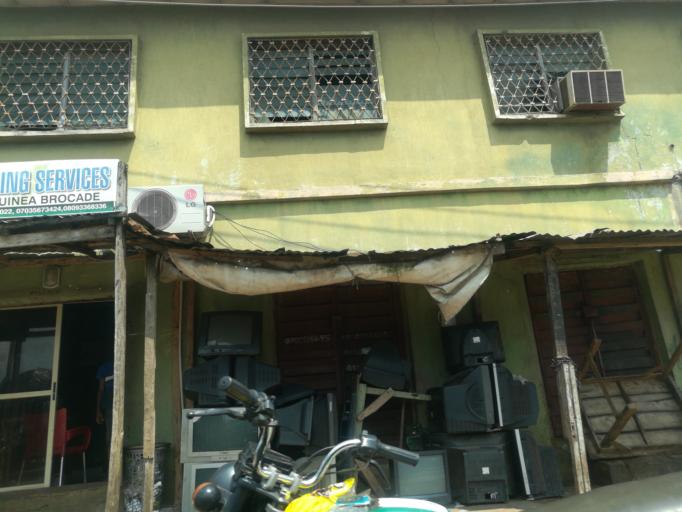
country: NG
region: Oyo
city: Ibadan
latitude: 7.4018
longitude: 3.8850
